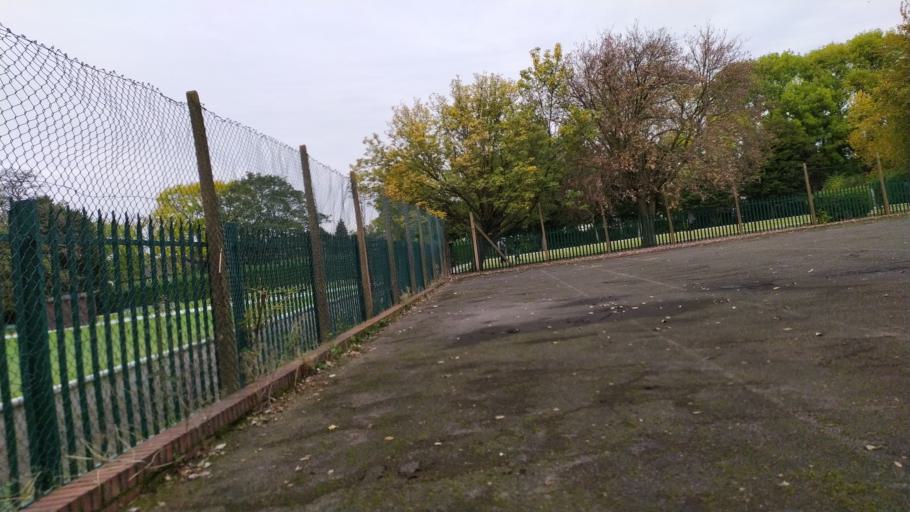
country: GB
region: England
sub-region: City and Borough of Leeds
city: Leeds
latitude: 53.8094
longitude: -1.5781
